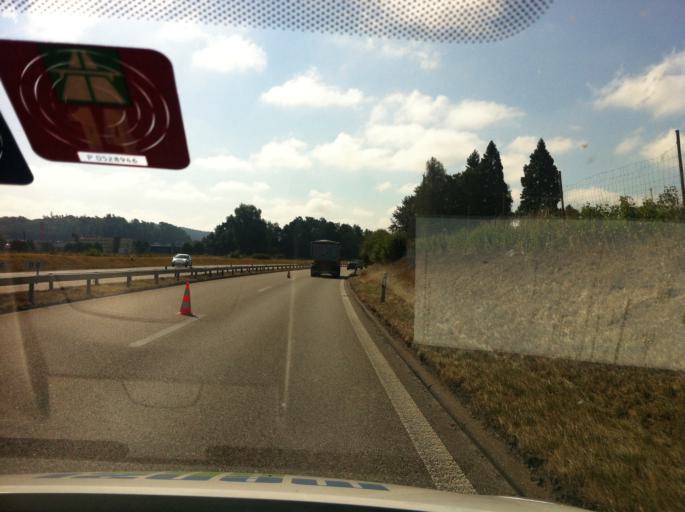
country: CH
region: Zurich
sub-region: Bezirk Buelach
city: Buelach / Niederflachs
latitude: 47.5075
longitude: 8.5320
